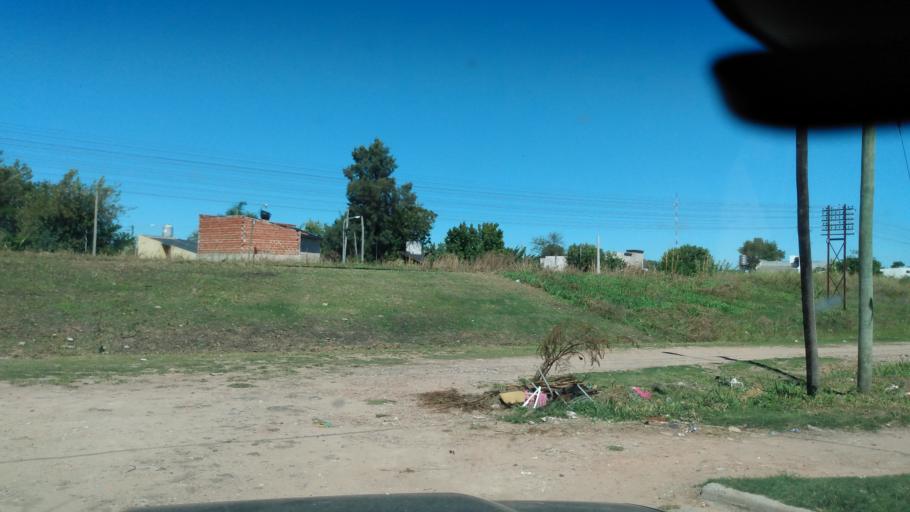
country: AR
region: Buenos Aires
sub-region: Partido de Lujan
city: Lujan
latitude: -34.5801
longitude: -59.1132
